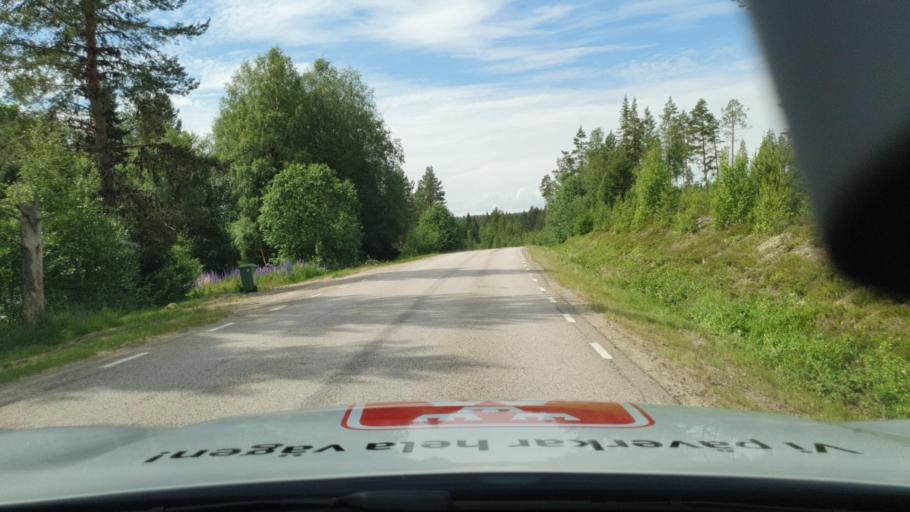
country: NO
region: Hedmark
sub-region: Grue
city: Kirkenaer
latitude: 60.6991
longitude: 12.5757
